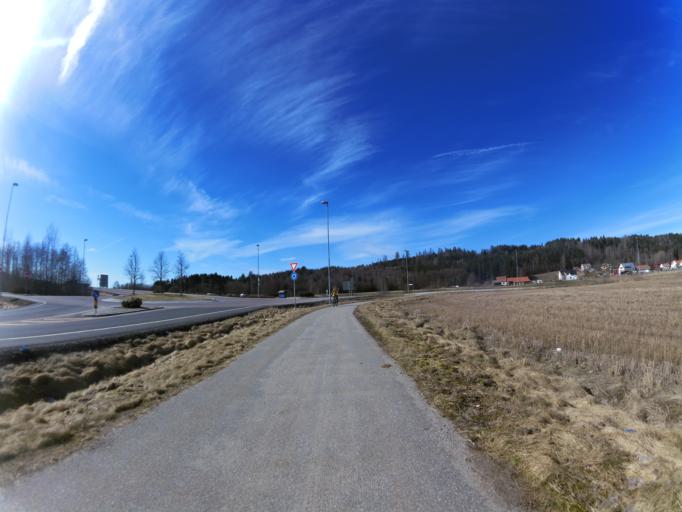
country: NO
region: Ostfold
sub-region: Rade
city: Karlshus
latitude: 59.3263
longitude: 10.9570
